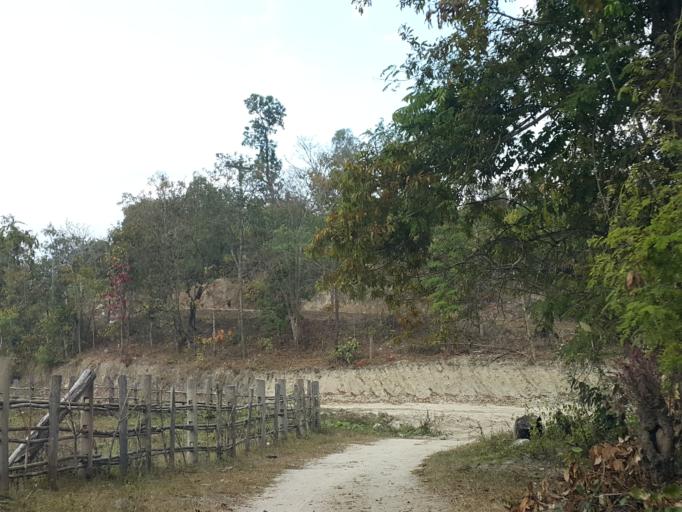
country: TH
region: Chiang Mai
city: Om Koi
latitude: 17.7979
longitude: 98.3418
